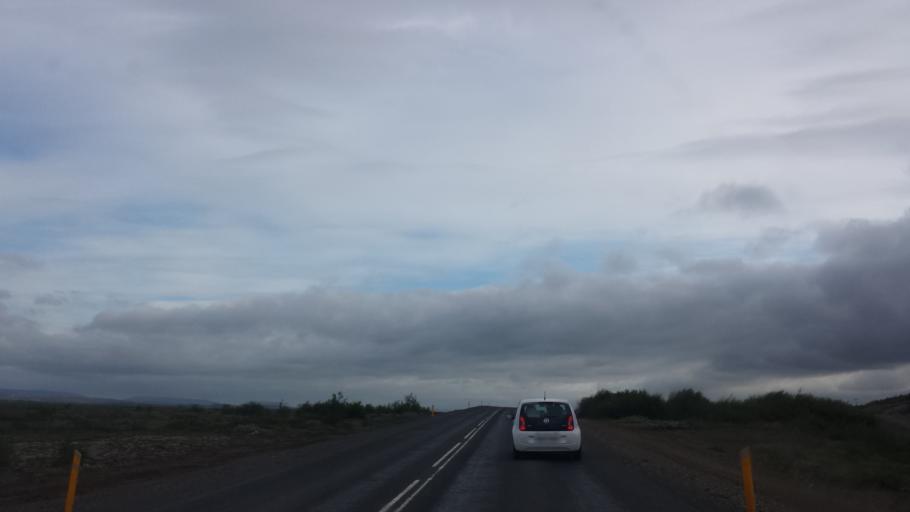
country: IS
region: South
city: Selfoss
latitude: 64.2878
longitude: -20.3392
